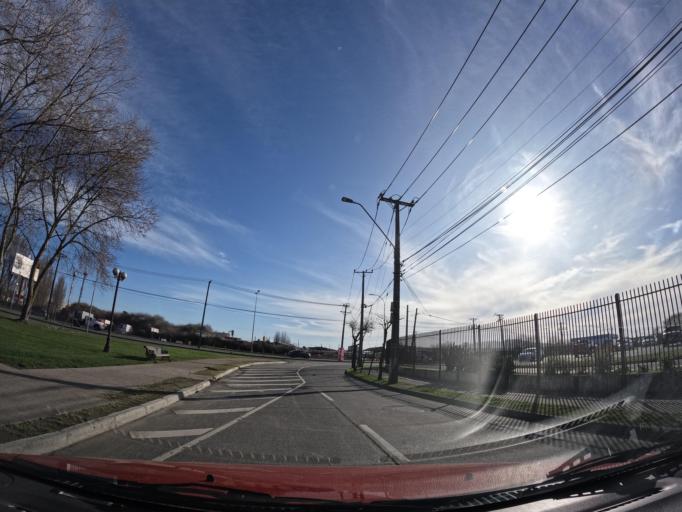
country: CL
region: Biobio
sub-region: Provincia de Concepcion
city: Concepcion
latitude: -36.7785
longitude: -73.0775
